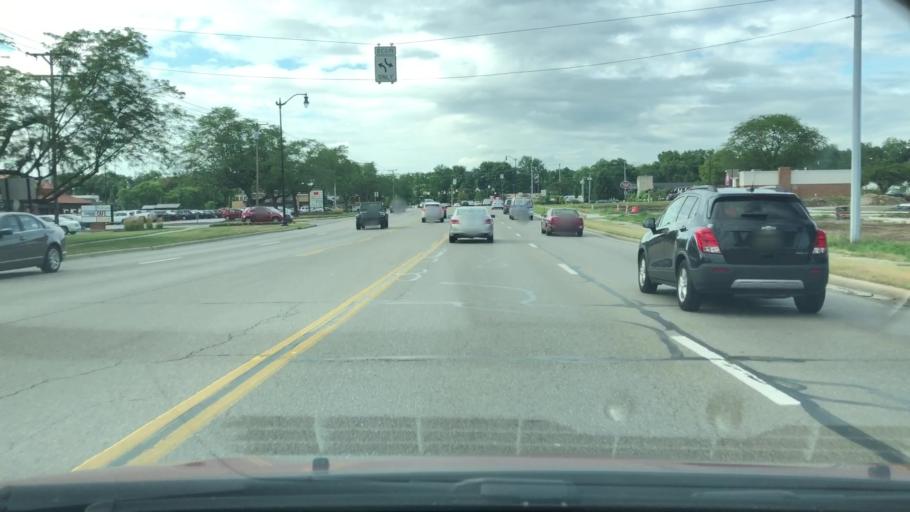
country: US
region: Ohio
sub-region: Montgomery County
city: Centerville
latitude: 39.6561
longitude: -84.1572
